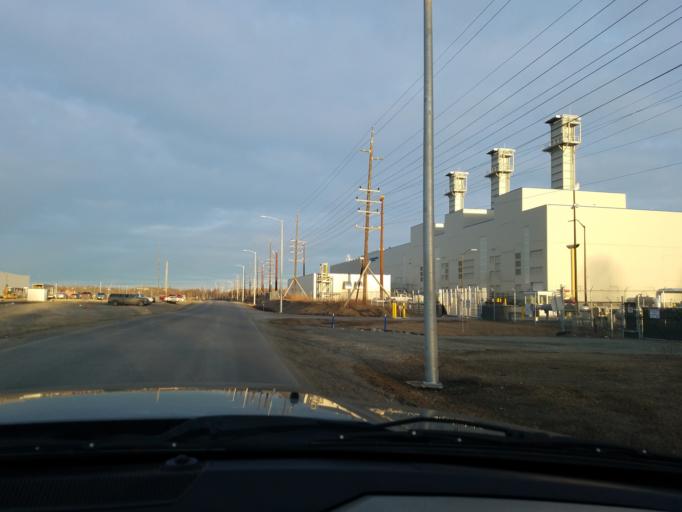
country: US
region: Alaska
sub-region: Anchorage Municipality
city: Anchorage
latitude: 61.1664
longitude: -149.9033
